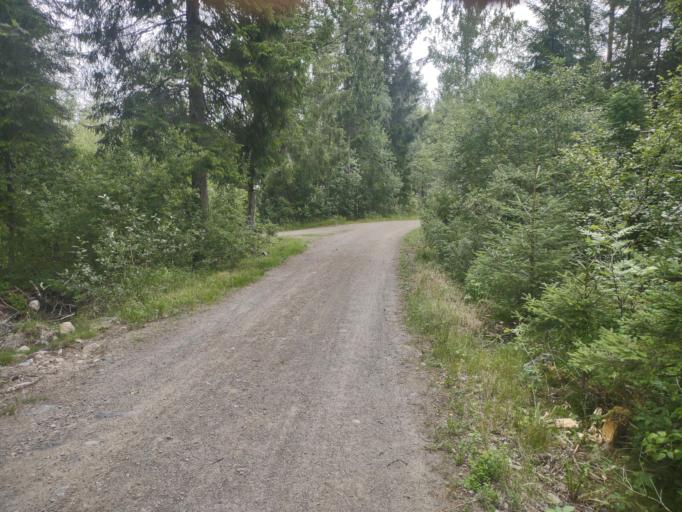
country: NO
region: Akershus
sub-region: Enebakk
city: Flateby
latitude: 59.8267
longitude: 11.1034
